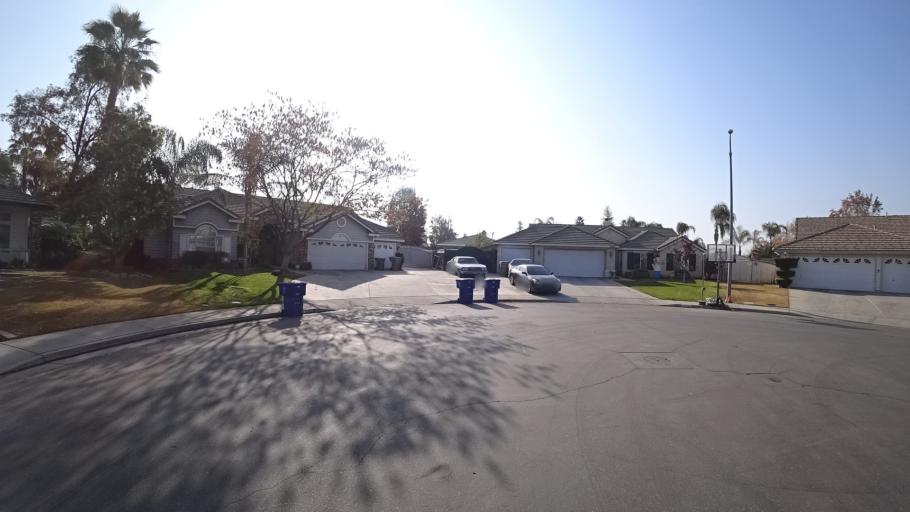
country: US
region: California
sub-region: Kern County
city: Greenacres
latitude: 35.4093
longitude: -119.1182
